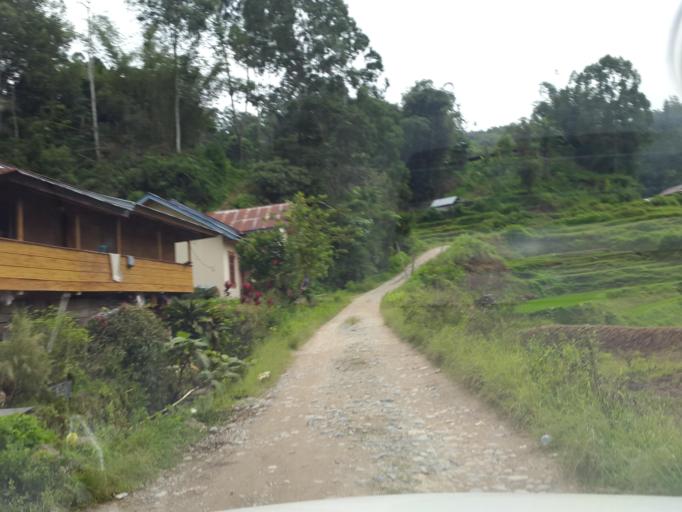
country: ID
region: South Sulawesi
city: Rantepang
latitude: -2.8662
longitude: 119.9489
